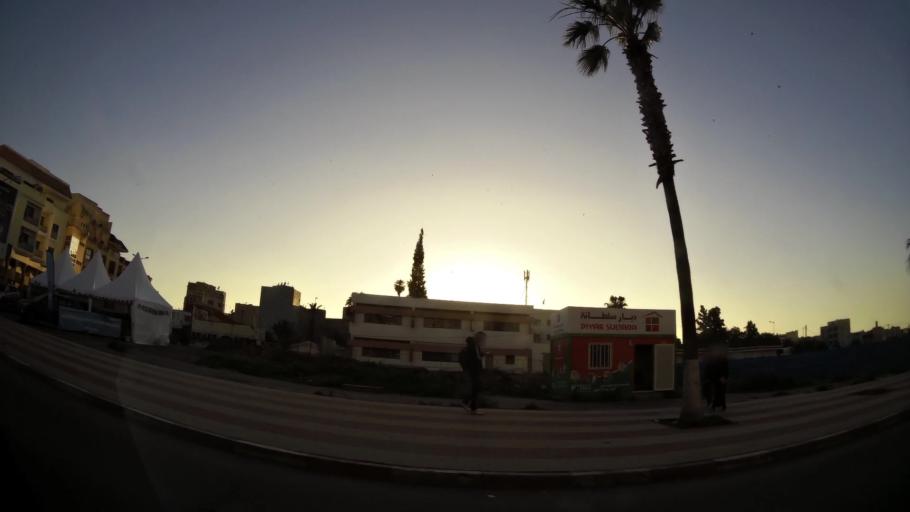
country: MA
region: Chaouia-Ouardigha
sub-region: Settat Province
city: Settat
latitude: 32.9984
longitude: -7.6204
